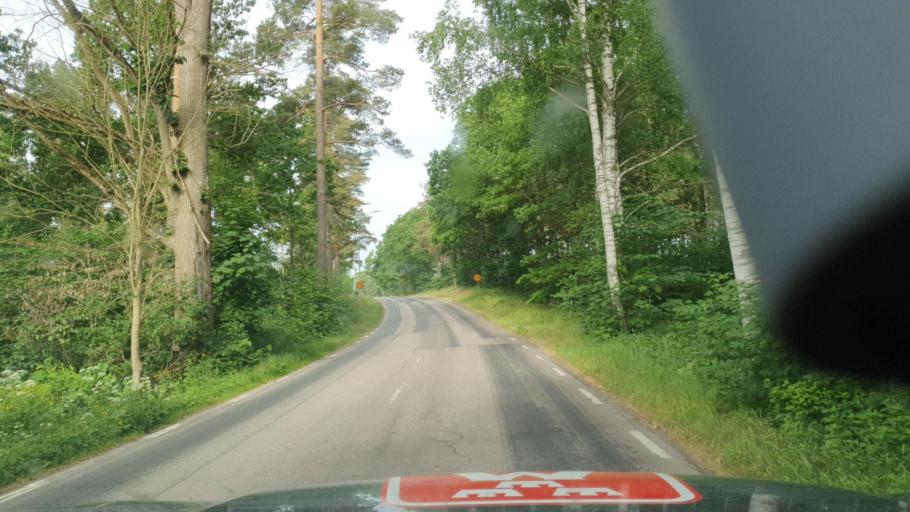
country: SE
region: Kalmar
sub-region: Kalmar Kommun
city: Ljungbyholm
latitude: 56.5923
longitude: 16.1377
